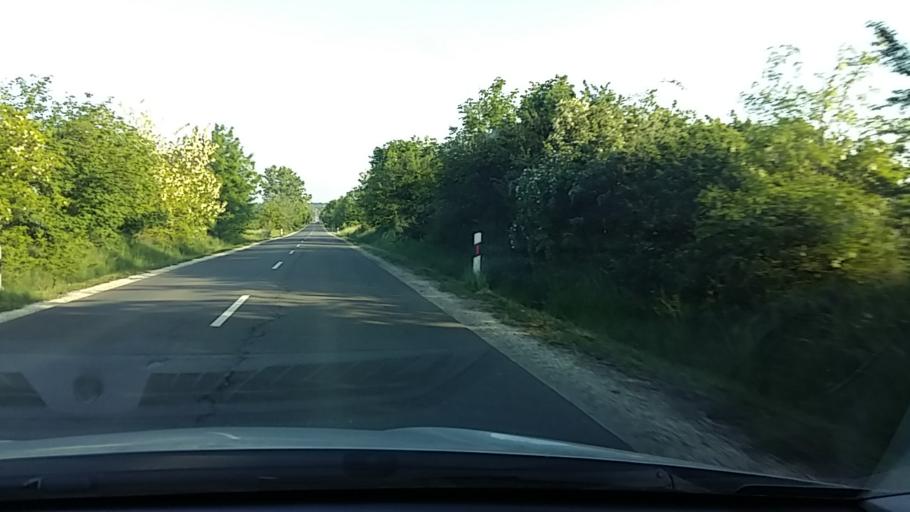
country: HU
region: Pest
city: Szod
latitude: 47.7282
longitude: 19.2256
